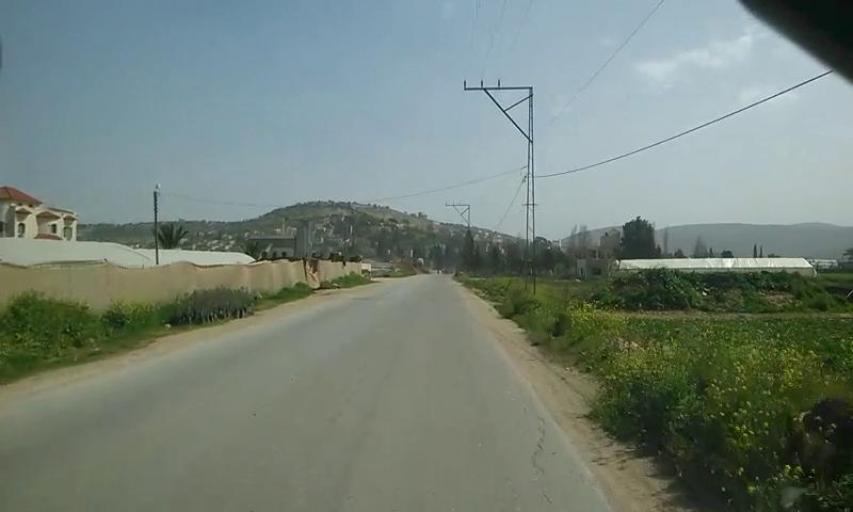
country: PS
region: West Bank
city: Ash Shuhada'
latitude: 32.4324
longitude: 35.2665
